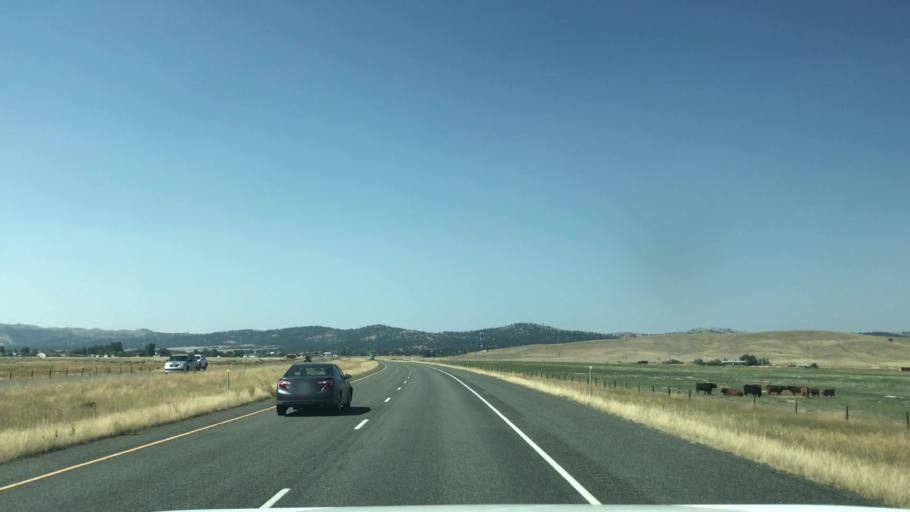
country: US
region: Montana
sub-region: Lewis and Clark County
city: Helena Valley Northwest
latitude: 46.7214
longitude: -112.0129
